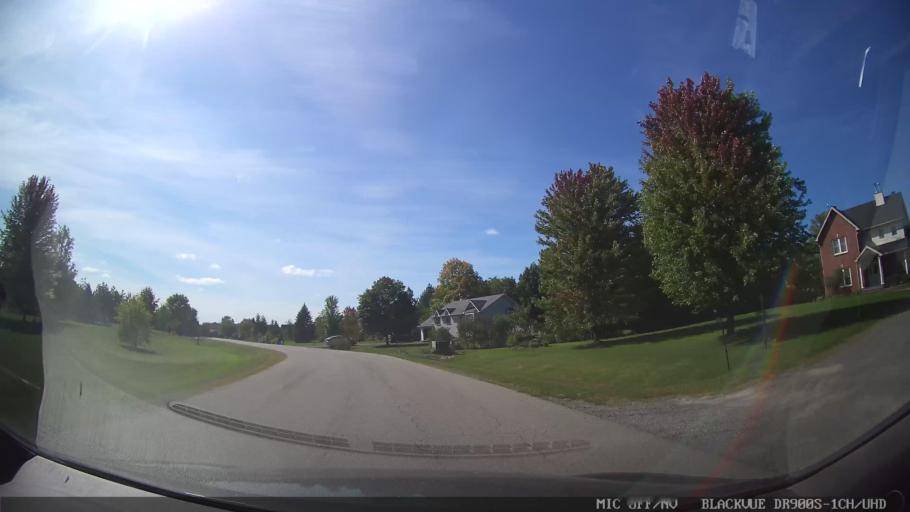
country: CA
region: Ontario
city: Bells Corners
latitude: 45.0945
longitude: -75.7346
